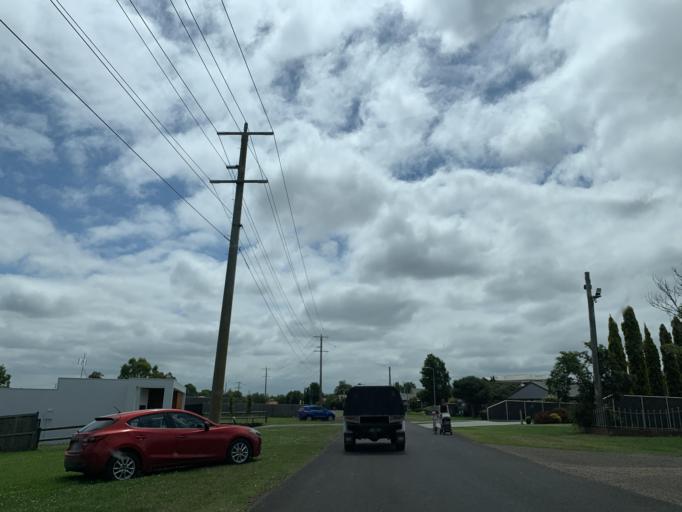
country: AU
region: Victoria
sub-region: Wellington
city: Sale
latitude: -38.1208
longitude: 147.0900
